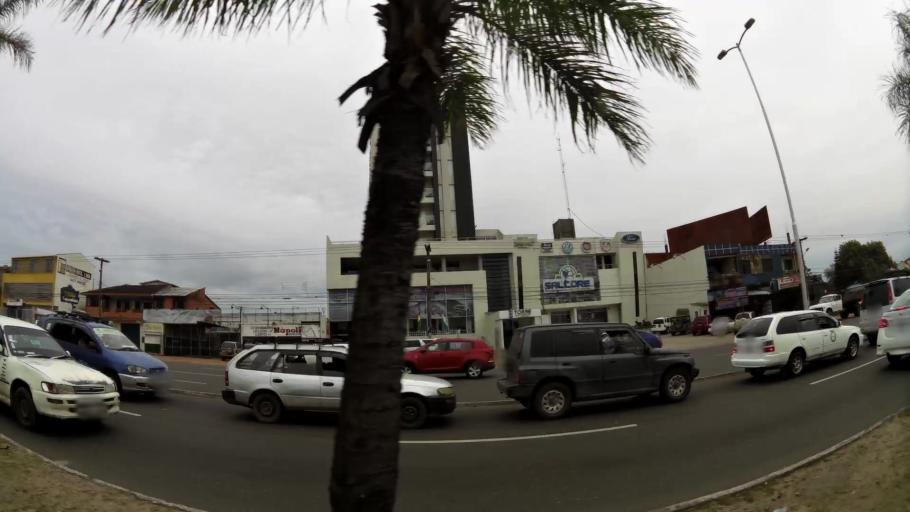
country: BO
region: Santa Cruz
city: Santa Cruz de la Sierra
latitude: -17.8010
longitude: -63.1881
